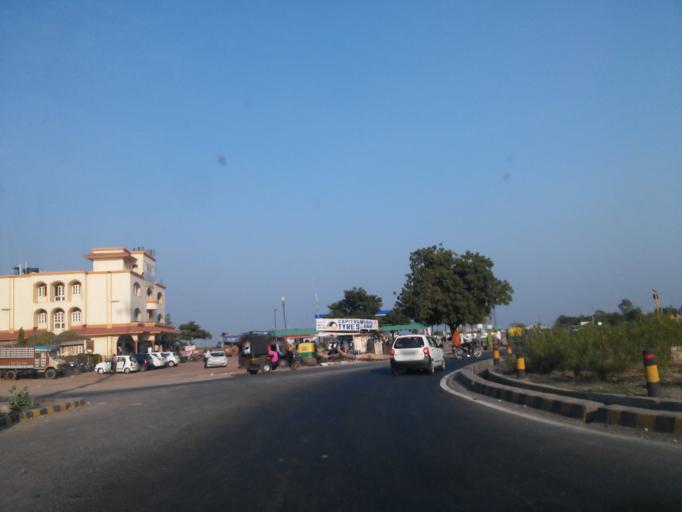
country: IN
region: Gujarat
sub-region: Ahmadabad
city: Mandal
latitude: 23.0980
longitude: 72.0627
